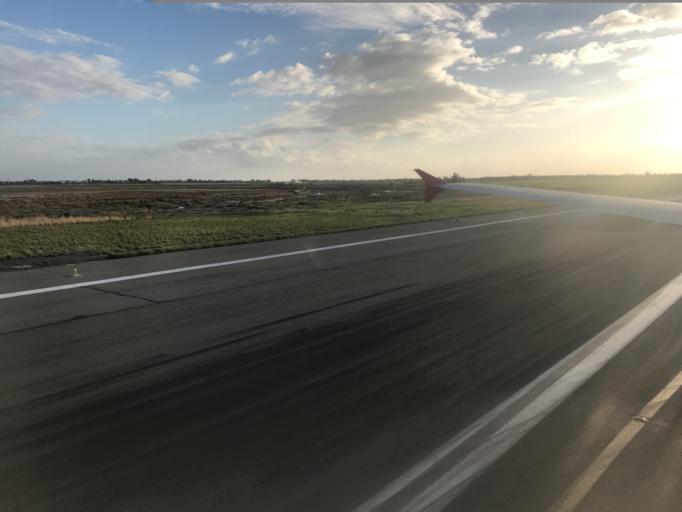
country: CY
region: Larnaka
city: Meneou
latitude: 34.8664
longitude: 33.6145
